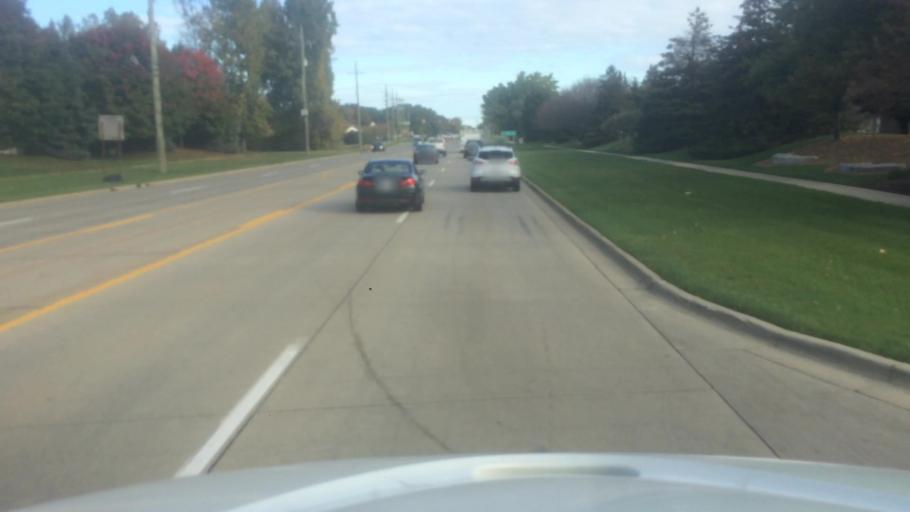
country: US
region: Michigan
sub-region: Macomb County
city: Shelby
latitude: 42.6530
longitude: -82.9939
